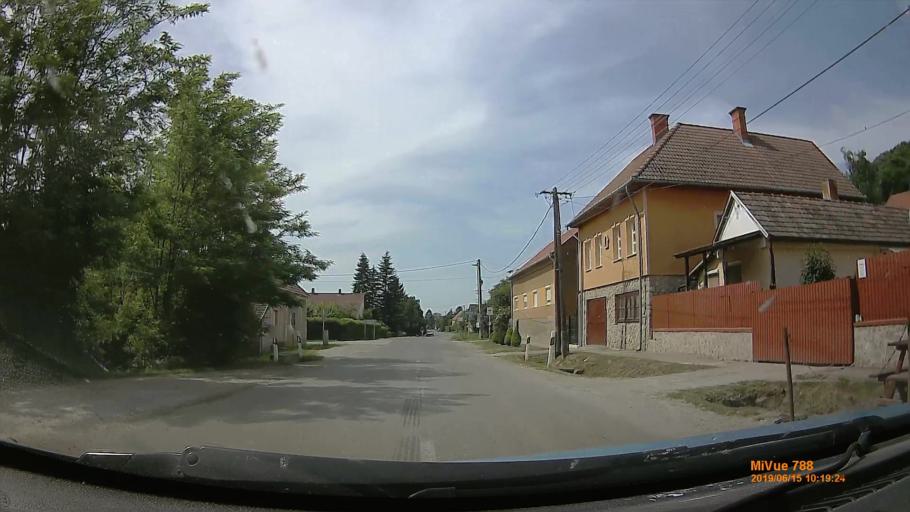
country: HU
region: Baranya
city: Buekkoesd
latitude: 46.1113
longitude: 17.9948
